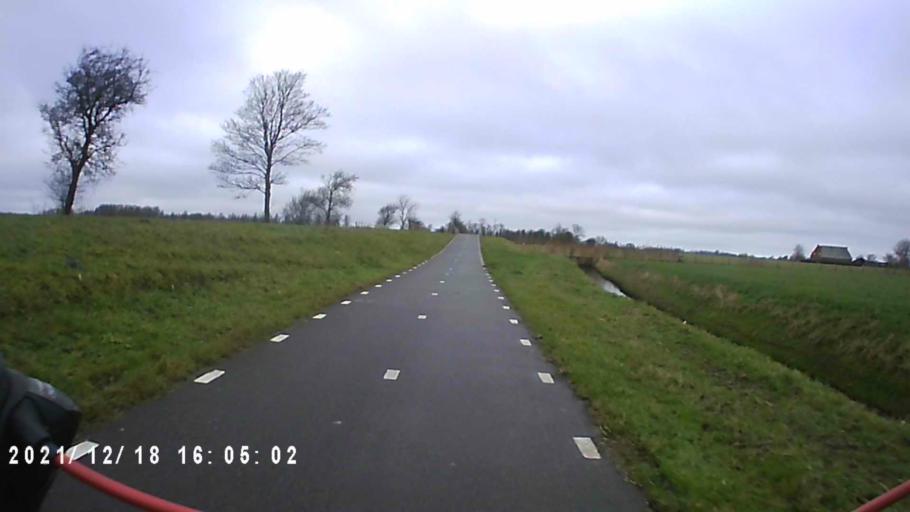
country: NL
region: Friesland
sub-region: Gemeente Dongeradeel
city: Anjum
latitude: 53.3529
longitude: 6.0772
